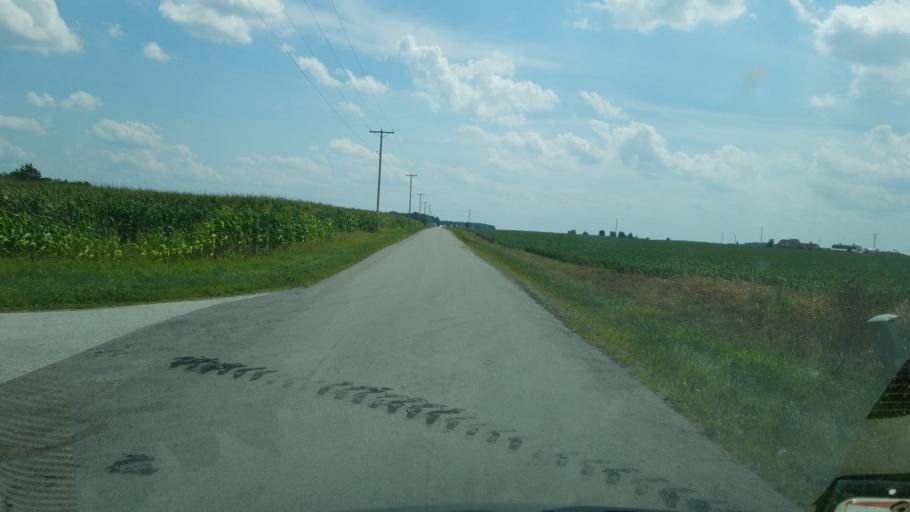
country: US
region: Ohio
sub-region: Hardin County
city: Forest
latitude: 40.7889
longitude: -83.4679
